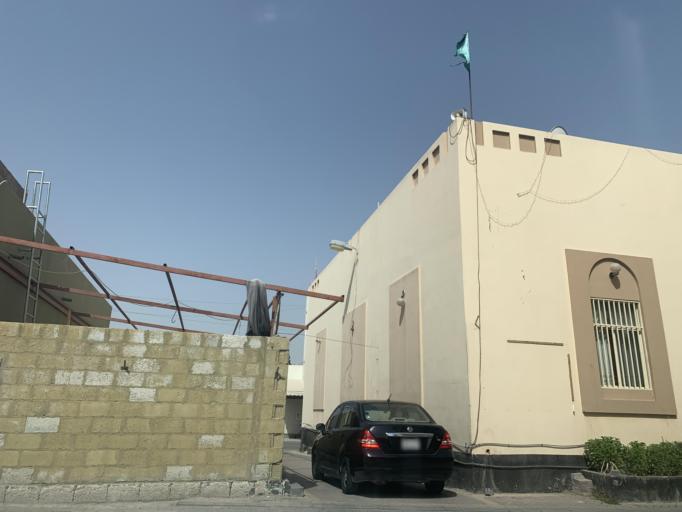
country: BH
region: Northern
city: Madinat `Isa
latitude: 26.1872
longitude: 50.5487
